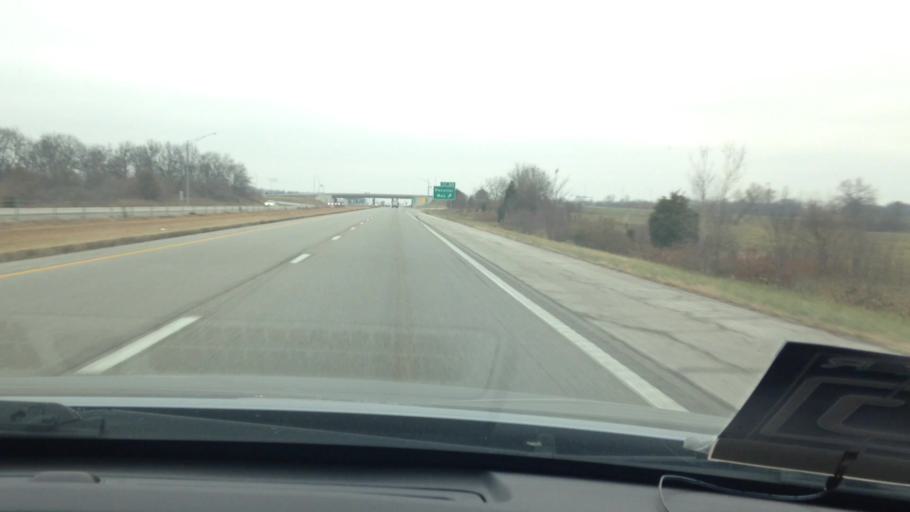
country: US
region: Missouri
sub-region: Cass County
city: Peculiar
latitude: 38.7351
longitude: -94.4661
